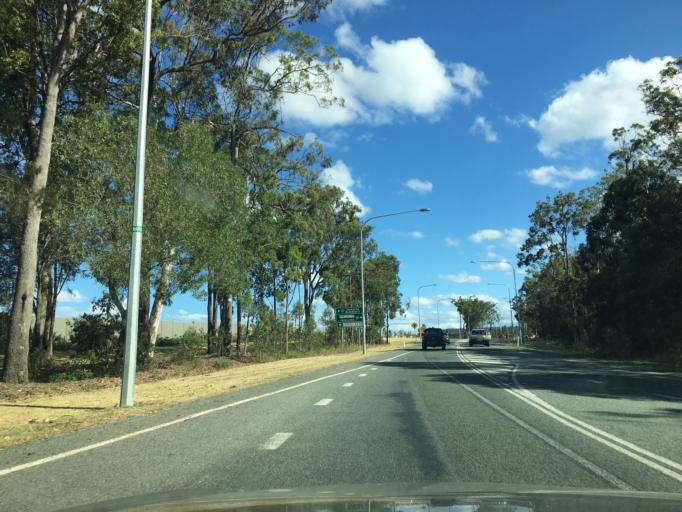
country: AU
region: Queensland
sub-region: Logan
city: Chambers Flat
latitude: -27.7972
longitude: 153.1003
